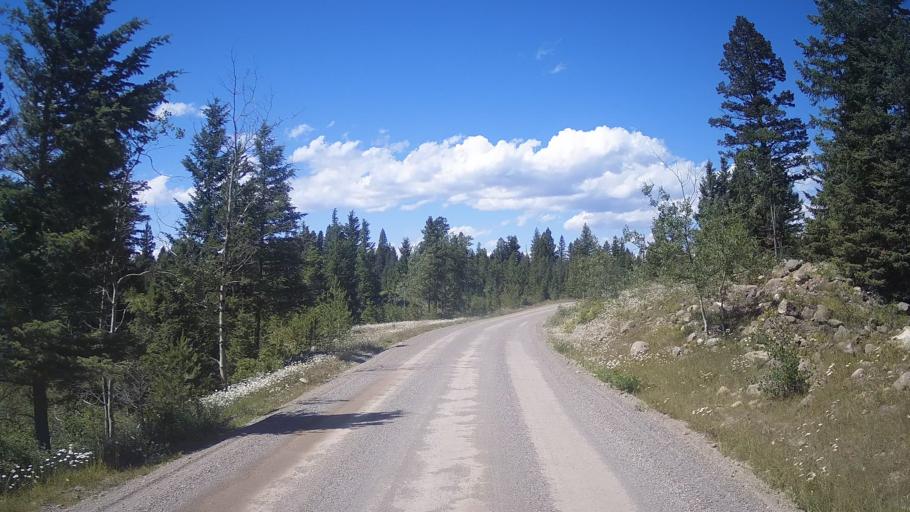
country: CA
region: British Columbia
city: Cache Creek
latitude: 51.1598
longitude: -121.5543
